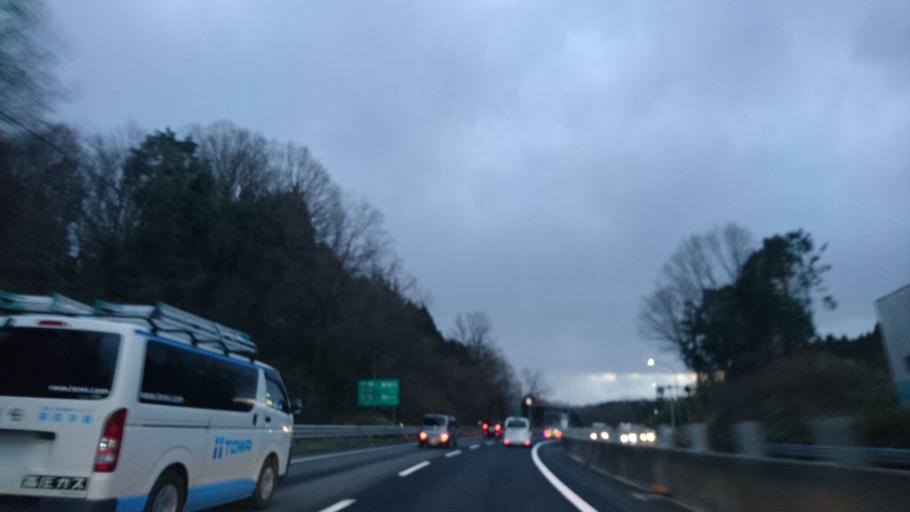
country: JP
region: Nara
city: Haibara-akanedai
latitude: 34.6222
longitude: 135.9828
